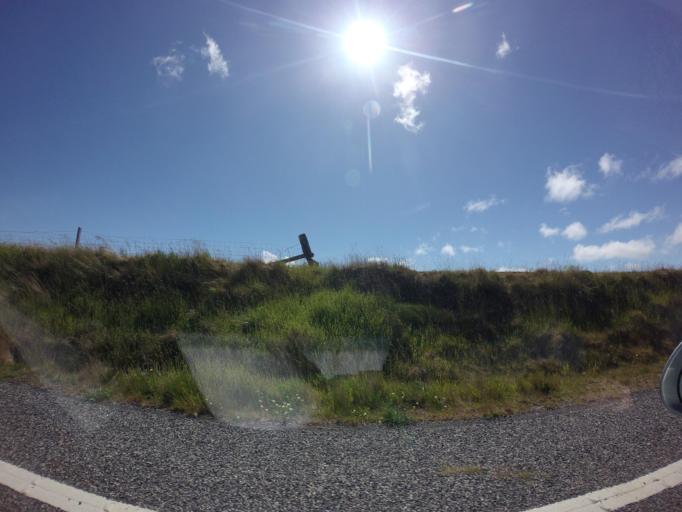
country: GB
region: Scotland
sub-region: Eilean Siar
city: Harris
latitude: 58.1934
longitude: -6.7143
